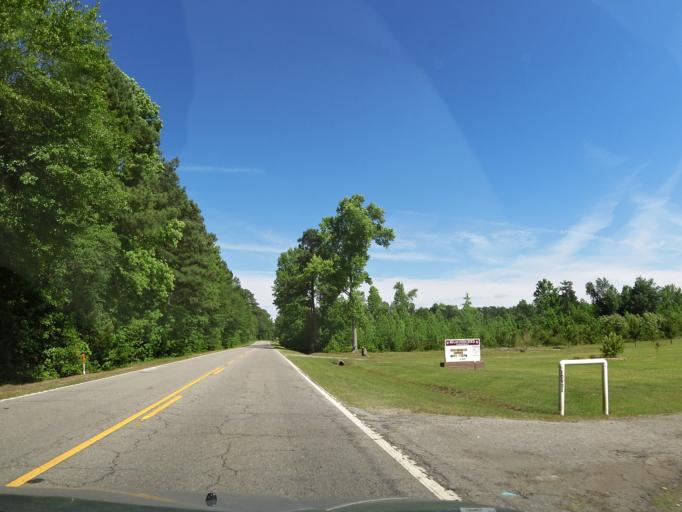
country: US
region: South Carolina
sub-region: Barnwell County
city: Williston
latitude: 33.3866
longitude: -81.3928
